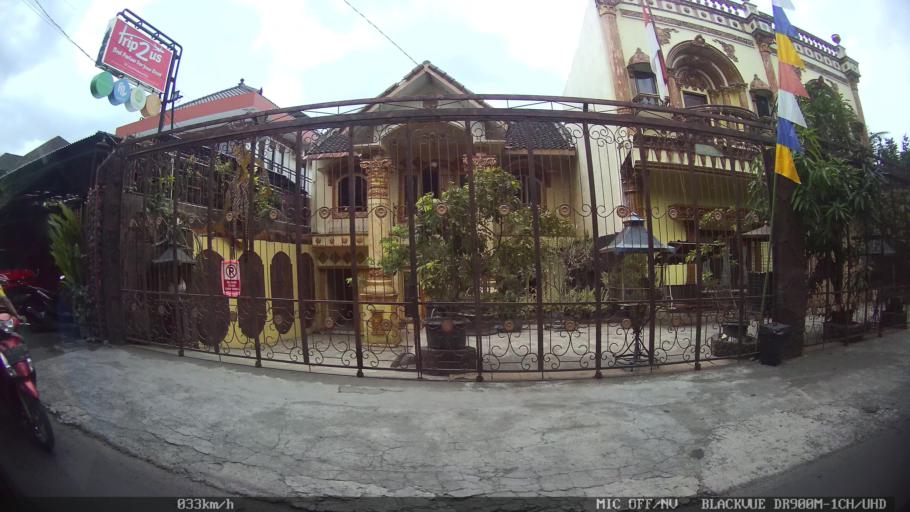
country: ID
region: Daerah Istimewa Yogyakarta
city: Depok
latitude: -7.8136
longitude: 110.4174
